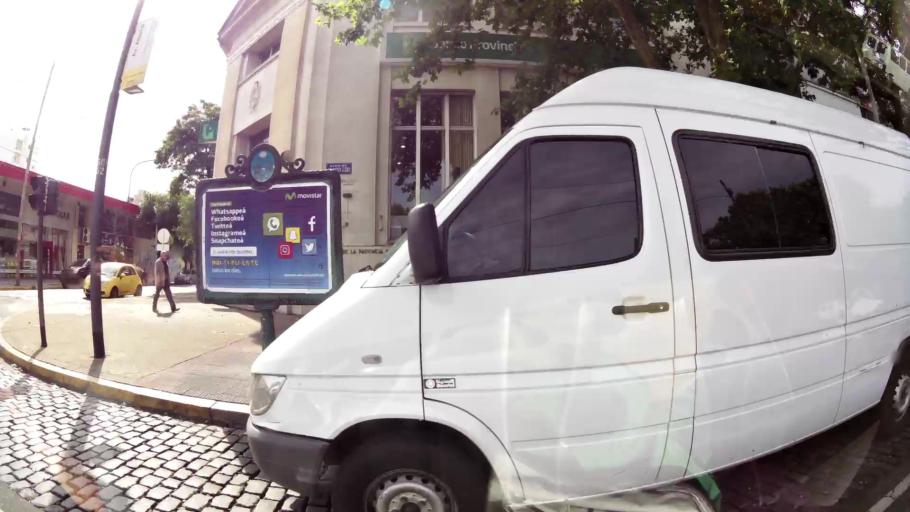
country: AR
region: Buenos Aires F.D.
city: Villa Lugano
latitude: -34.6549
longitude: -58.5065
